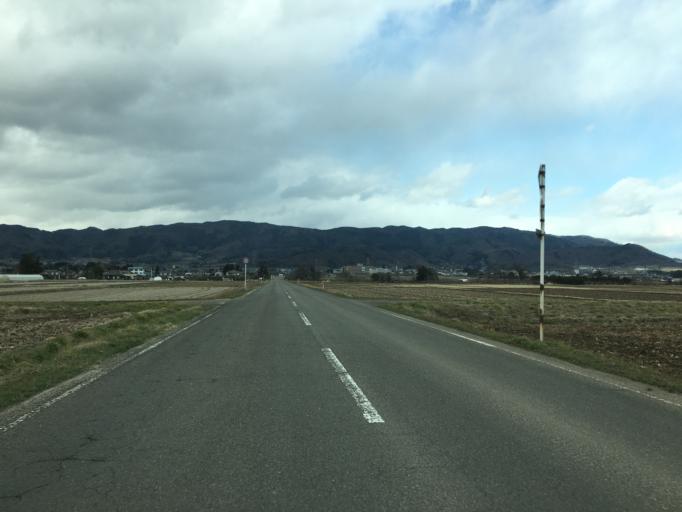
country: JP
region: Fukushima
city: Hobaramachi
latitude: 37.8574
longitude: 140.5381
